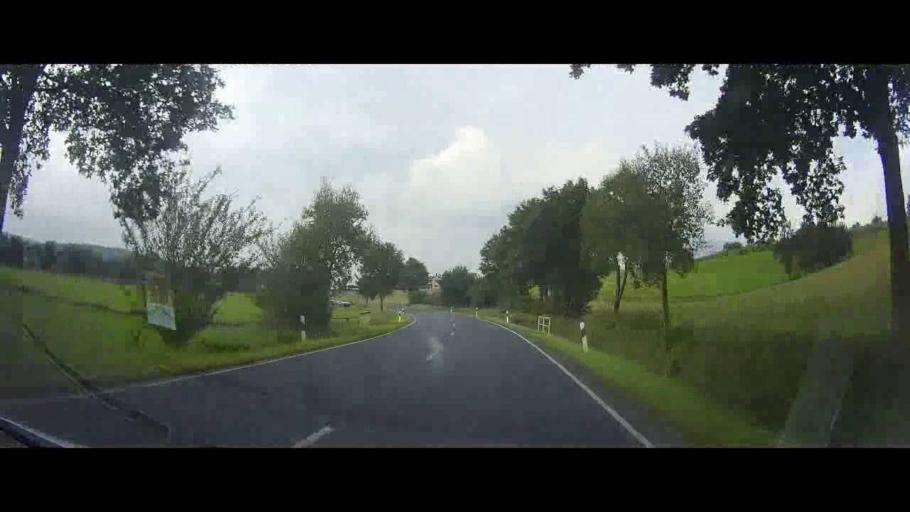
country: DE
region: Lower Saxony
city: Adelebsen
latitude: 51.5815
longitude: 9.7016
